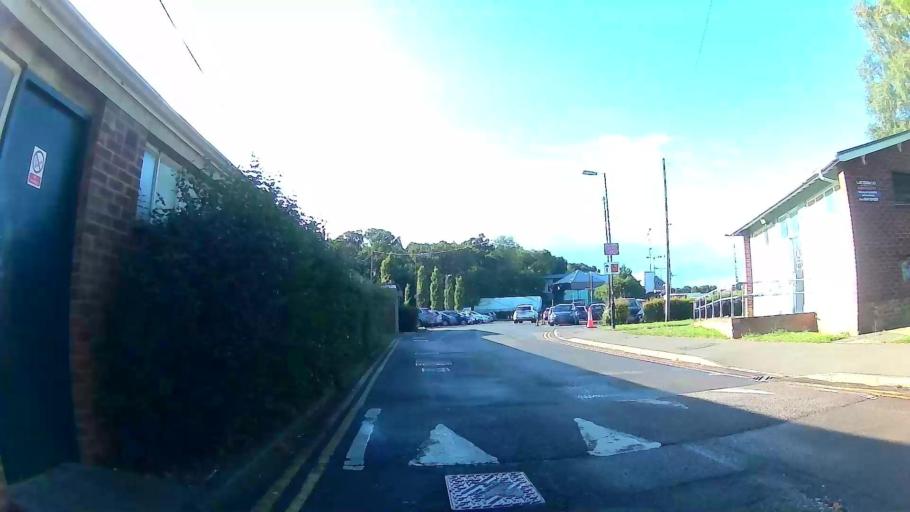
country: GB
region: England
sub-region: Essex
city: Chelmsford
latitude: 51.7516
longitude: 0.4507
